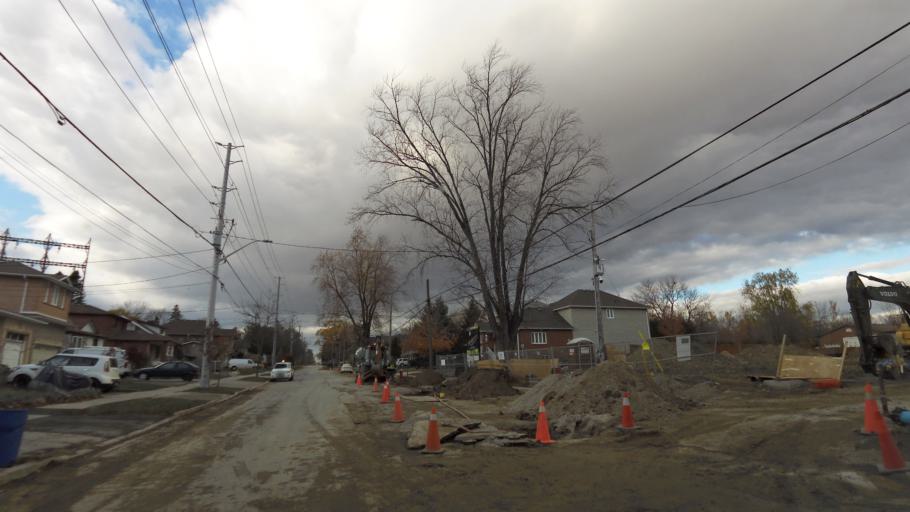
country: CA
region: Ontario
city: Etobicoke
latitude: 43.5832
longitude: -79.5602
